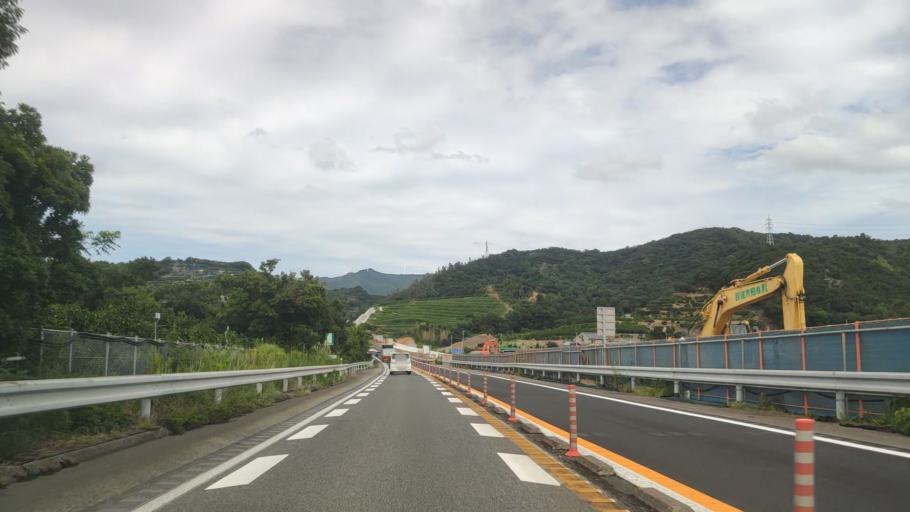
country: JP
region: Wakayama
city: Gobo
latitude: 33.9129
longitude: 135.1944
